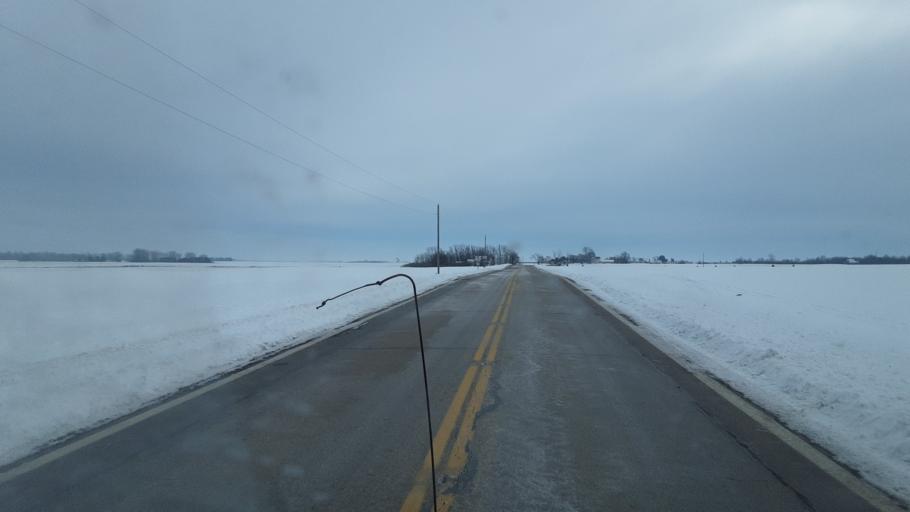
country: US
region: Ohio
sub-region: Champaign County
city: Mechanicsburg
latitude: 40.0237
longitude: -83.5202
